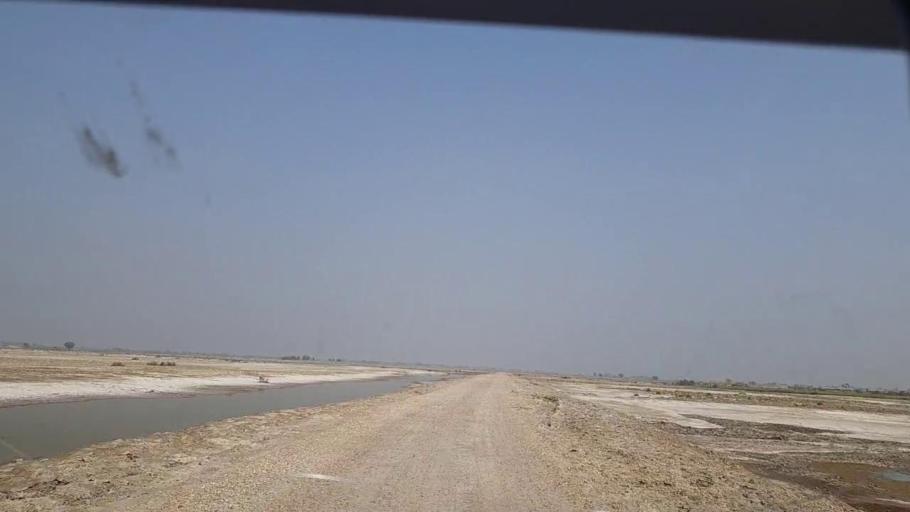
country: PK
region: Sindh
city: Shikarpur
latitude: 28.0485
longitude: 68.6543
